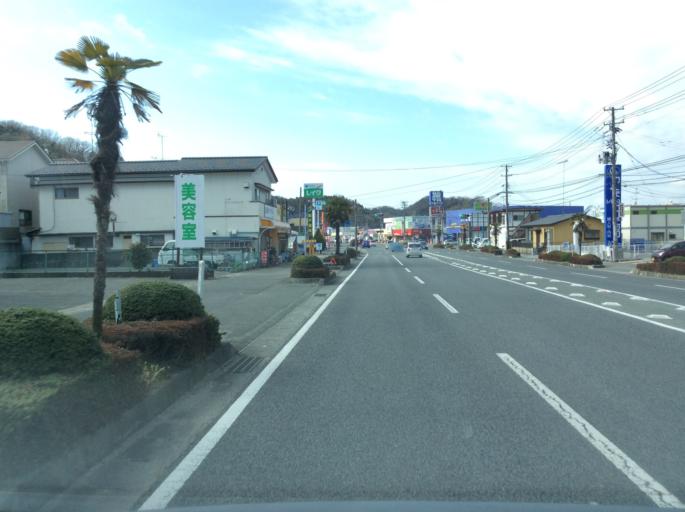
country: JP
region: Fukushima
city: Iwaki
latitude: 36.9853
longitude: 140.9021
